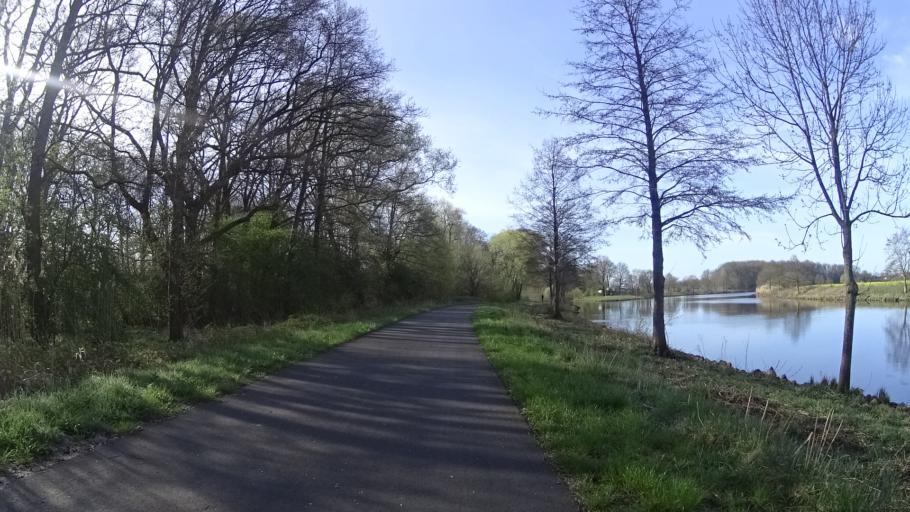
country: DE
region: Lower Saxony
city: Haren
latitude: 52.7996
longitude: 7.2622
